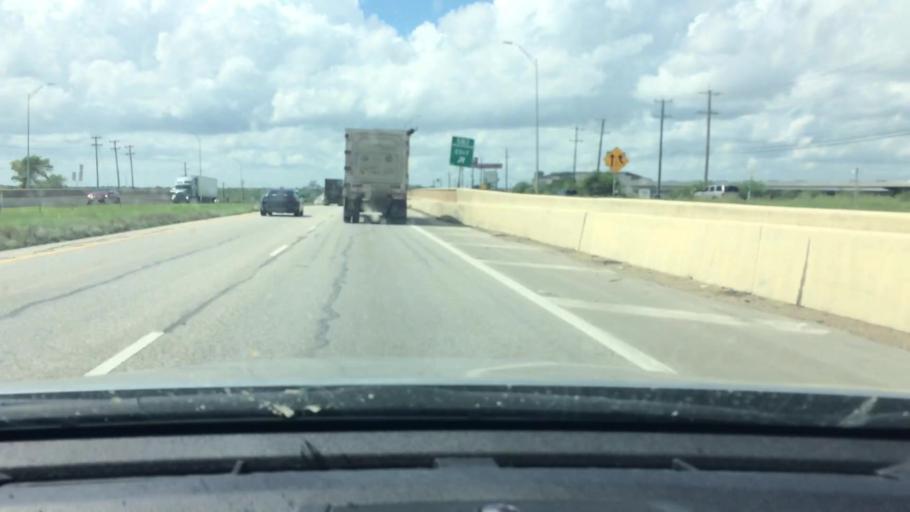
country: US
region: Texas
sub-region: Bexar County
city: Kirby
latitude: 29.4444
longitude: -98.3634
